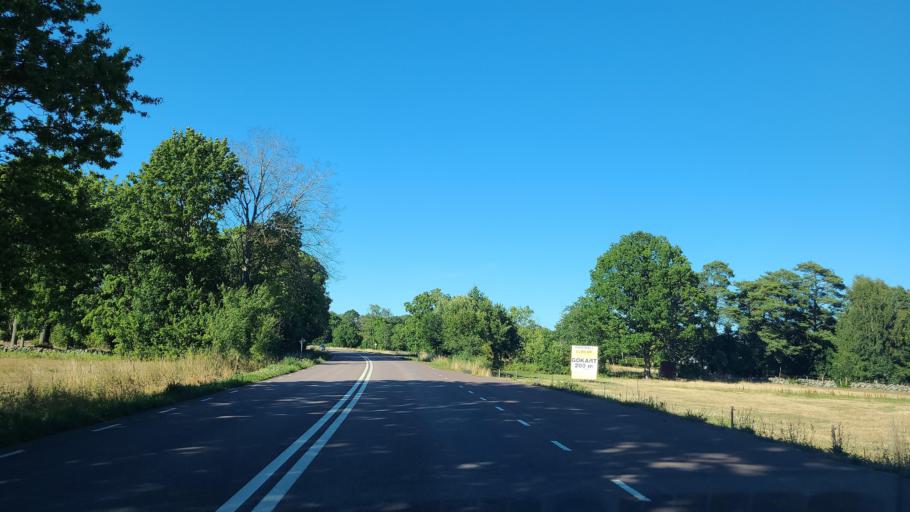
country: SE
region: Kalmar
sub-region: Borgholms Kommun
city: Borgholm
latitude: 57.1983
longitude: 17.0435
